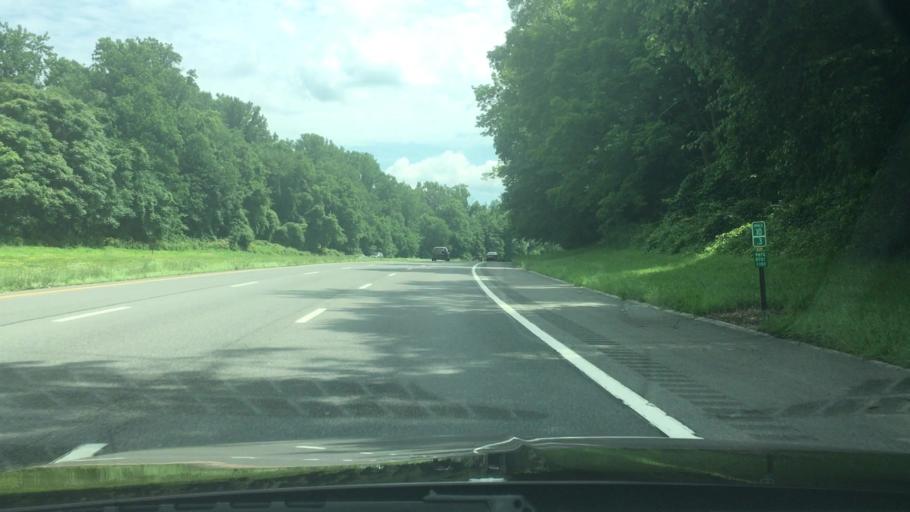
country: US
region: New York
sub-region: Westchester County
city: Briarcliff Manor
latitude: 41.2041
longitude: -73.8085
